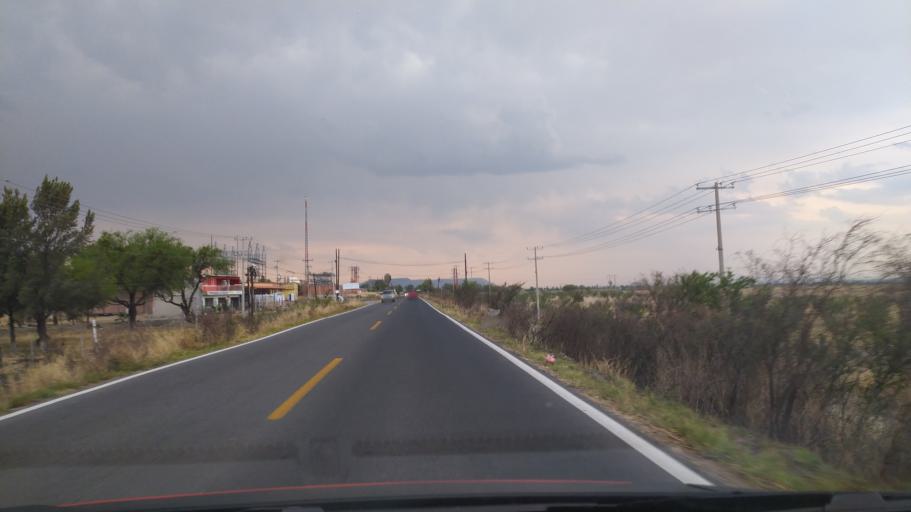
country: MX
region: Guanajuato
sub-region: San Francisco del Rincon
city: San Ignacio de Hidalgo
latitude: 20.8239
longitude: -101.9017
